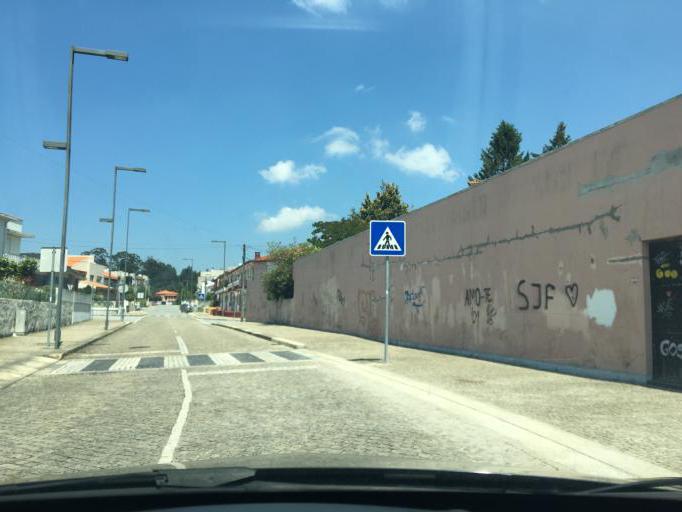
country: PT
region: Porto
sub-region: Maia
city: Anta
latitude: 41.2631
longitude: -8.6172
